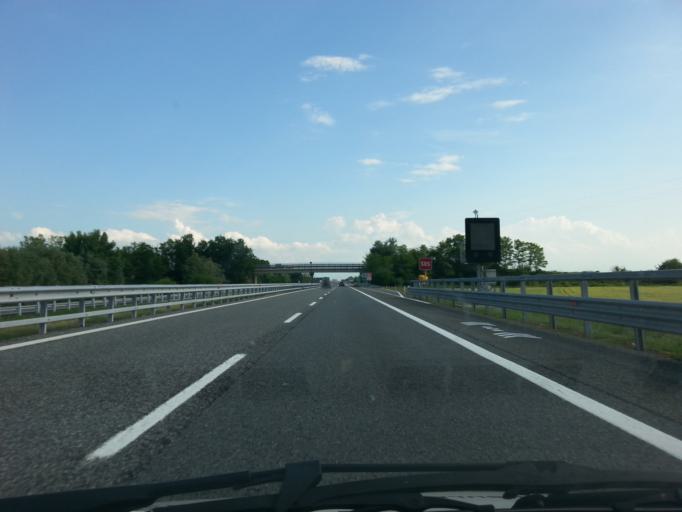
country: IT
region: Piedmont
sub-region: Provincia di Cuneo
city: Sanfre
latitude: 44.7245
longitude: 7.7571
